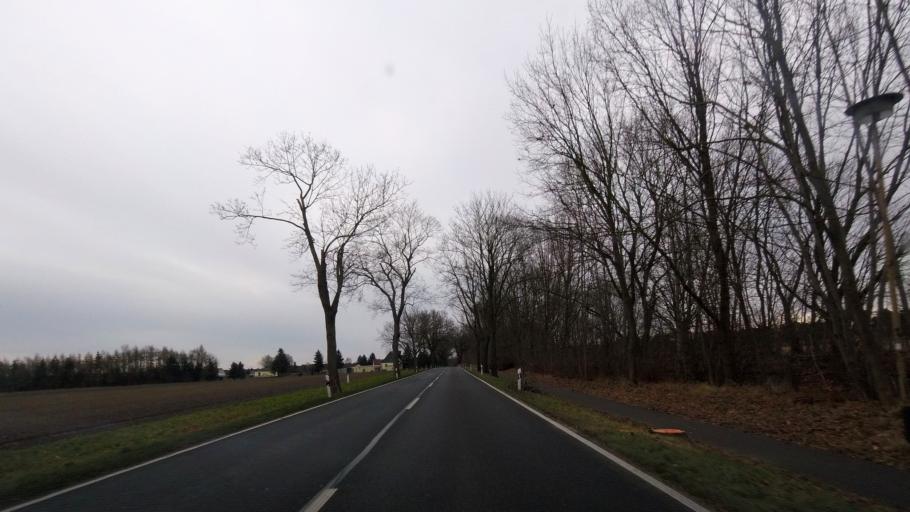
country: DE
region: Brandenburg
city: Treuenbrietzen
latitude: 52.0857
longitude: 12.8776
